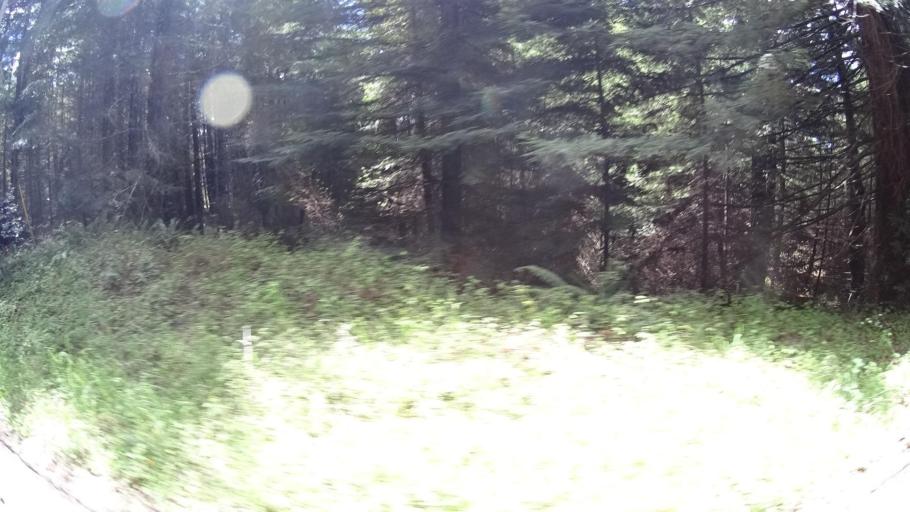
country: US
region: California
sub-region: Humboldt County
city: Blue Lake
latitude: 40.8166
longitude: -123.8908
